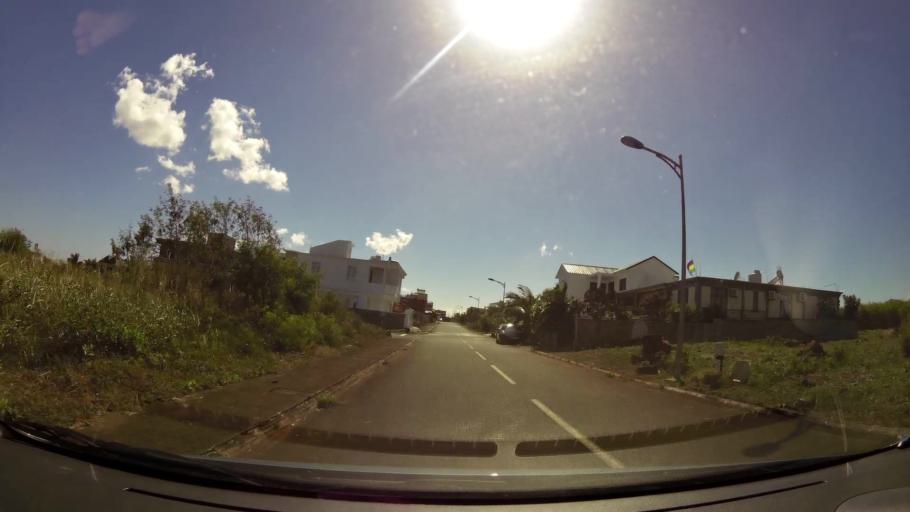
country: MU
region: Black River
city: Flic en Flac
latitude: -20.2847
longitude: 57.3774
